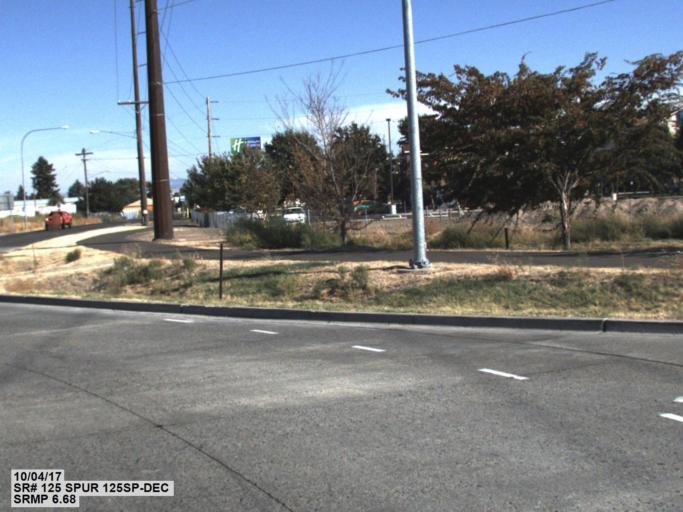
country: US
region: Washington
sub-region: Walla Walla County
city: College Place
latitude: 46.0090
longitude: -118.3903
